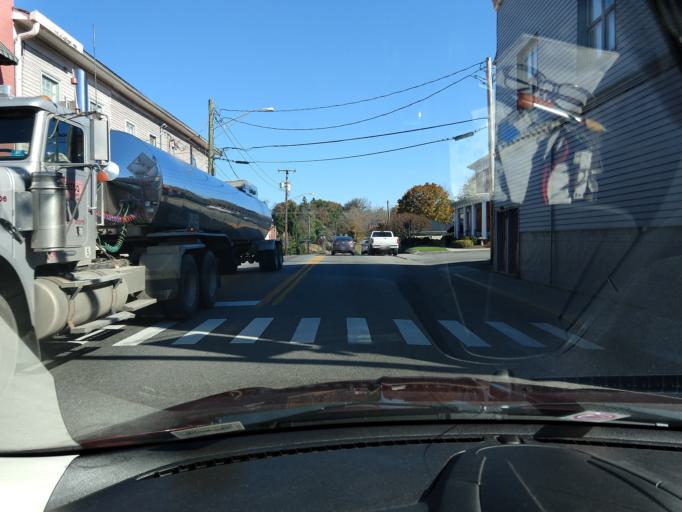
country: US
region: West Virginia
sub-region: Greenbrier County
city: Lewisburg
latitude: 37.8018
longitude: -80.4453
